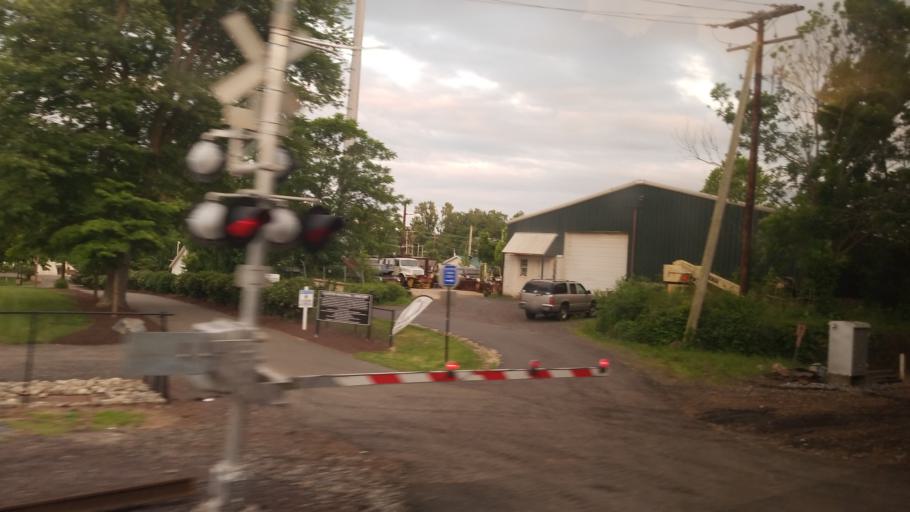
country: US
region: Virginia
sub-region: Culpeper County
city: Culpeper
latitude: 38.4707
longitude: -77.9941
